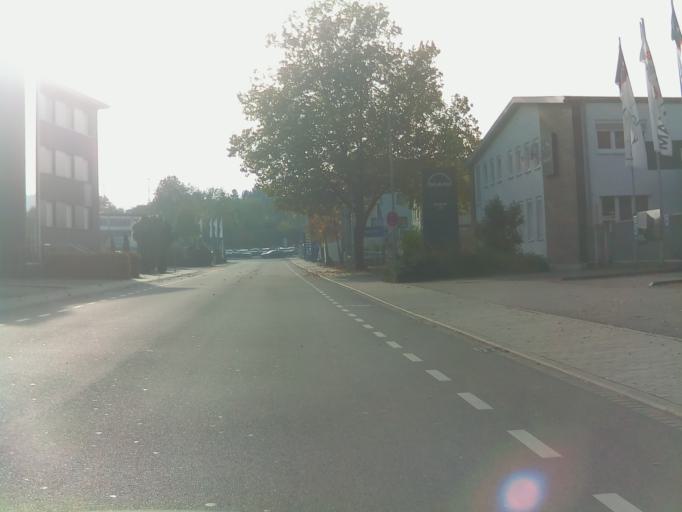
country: DE
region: Baden-Wuerttemberg
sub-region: Karlsruhe Region
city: Neckarzimmern
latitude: 49.3438
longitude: 9.1245
